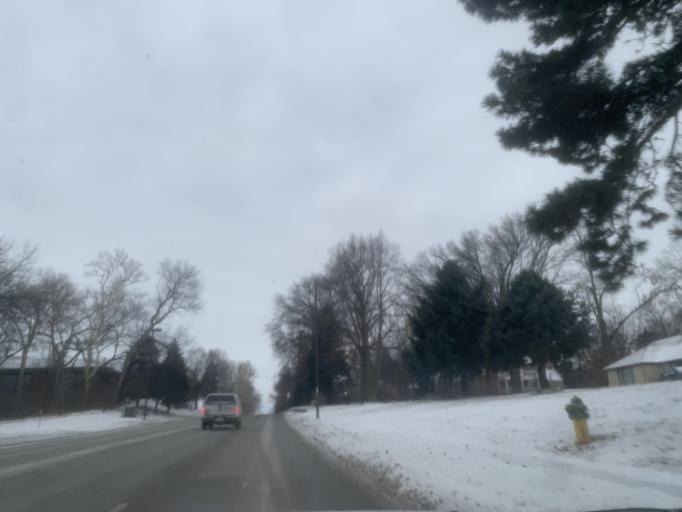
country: US
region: Nebraska
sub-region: Douglas County
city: Ralston
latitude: 41.2604
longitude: -96.0526
